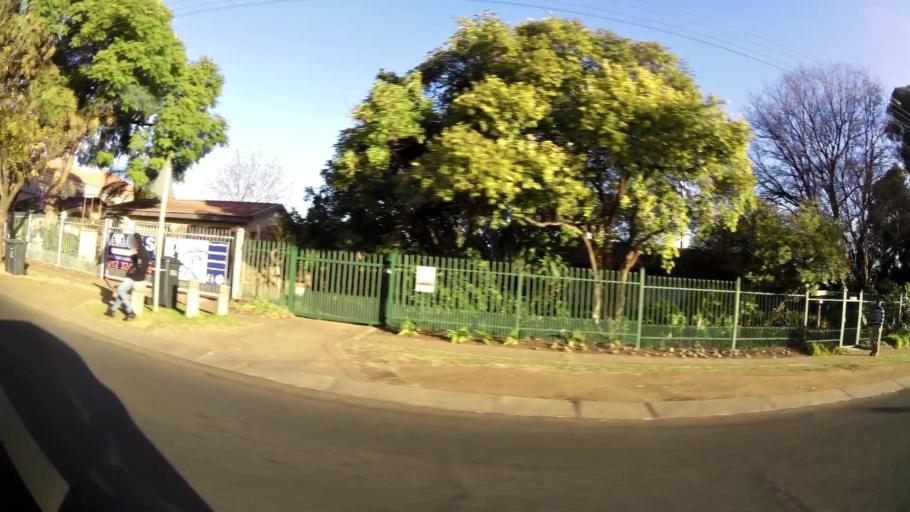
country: ZA
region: Gauteng
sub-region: City of Tshwane Metropolitan Municipality
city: Pretoria
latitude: -25.7045
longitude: 28.2398
